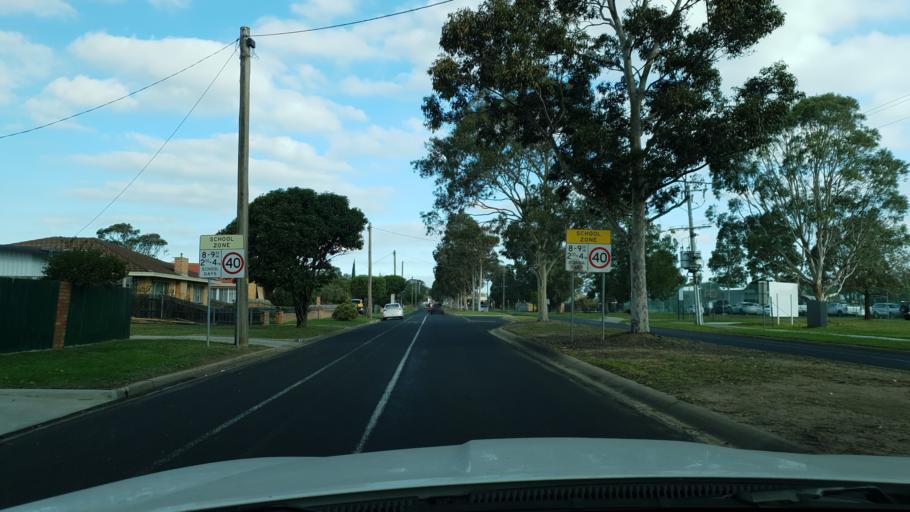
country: AU
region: Victoria
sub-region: East Gippsland
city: Bairnsdale
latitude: -37.8272
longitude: 147.6070
